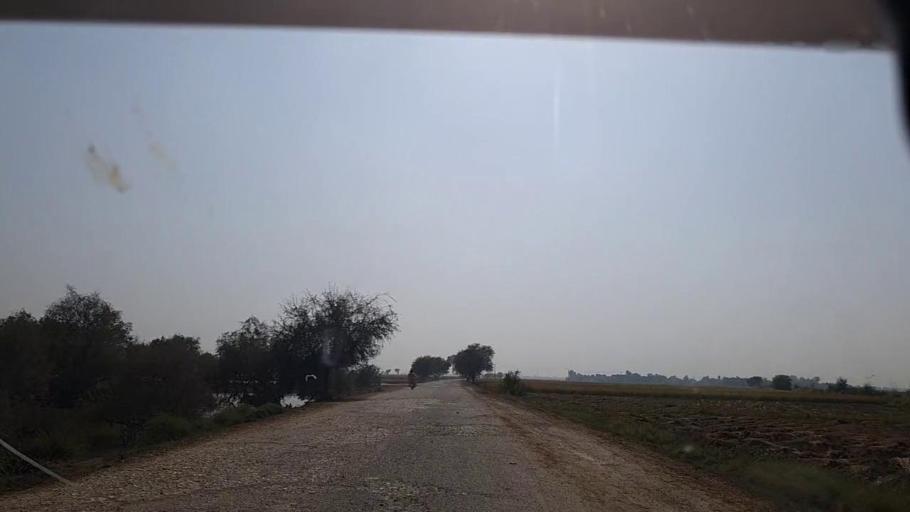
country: PK
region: Sindh
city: Shikarpur
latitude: 28.0968
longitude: 68.6106
